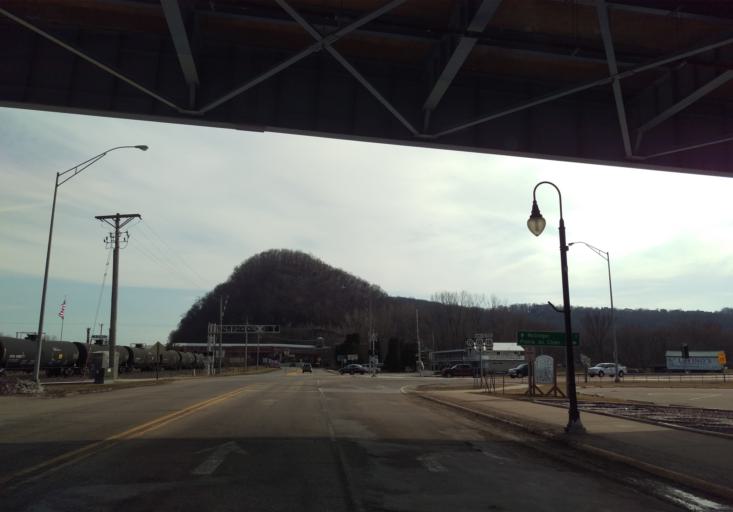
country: US
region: Wisconsin
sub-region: Crawford County
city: Prairie du Chien
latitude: 43.0440
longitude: -91.1782
